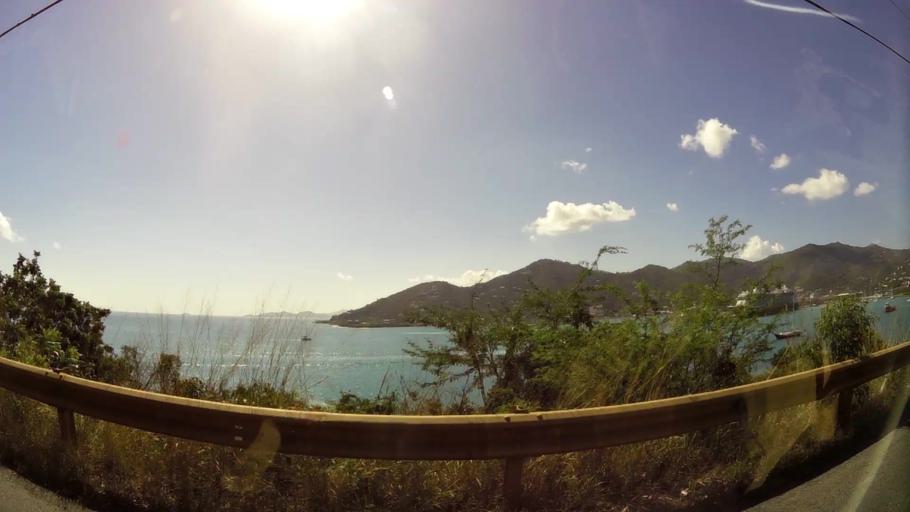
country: VG
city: Tortola
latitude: 18.4203
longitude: -64.6032
